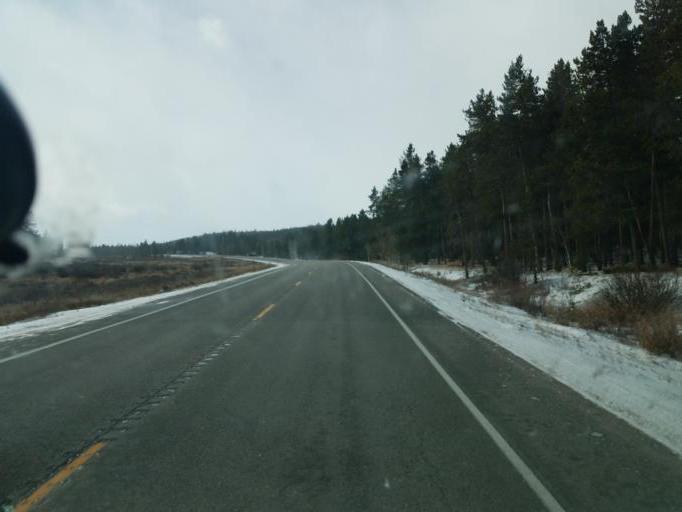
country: US
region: Colorado
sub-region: Summit County
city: Breckenridge
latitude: 39.4229
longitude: -105.7652
